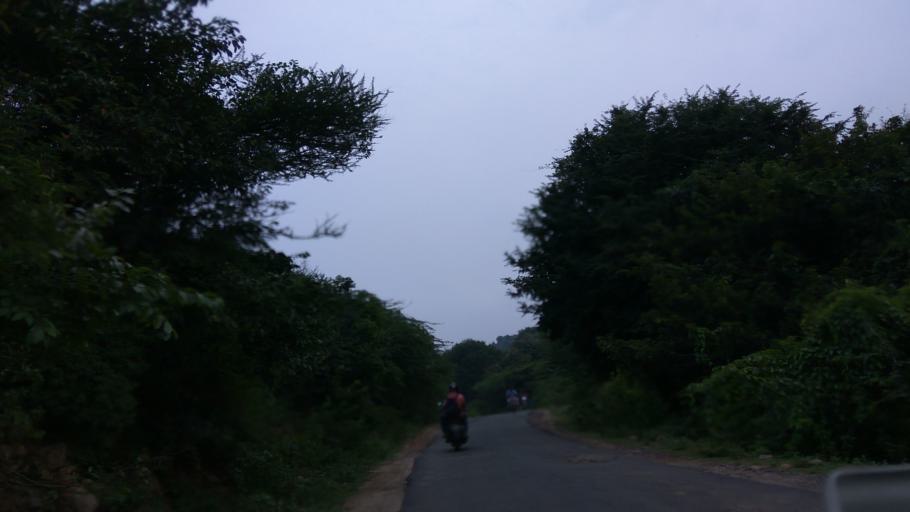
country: IN
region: Tamil Nadu
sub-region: Dharmapuri
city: Dharmapuri
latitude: 12.0137
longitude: 78.1291
